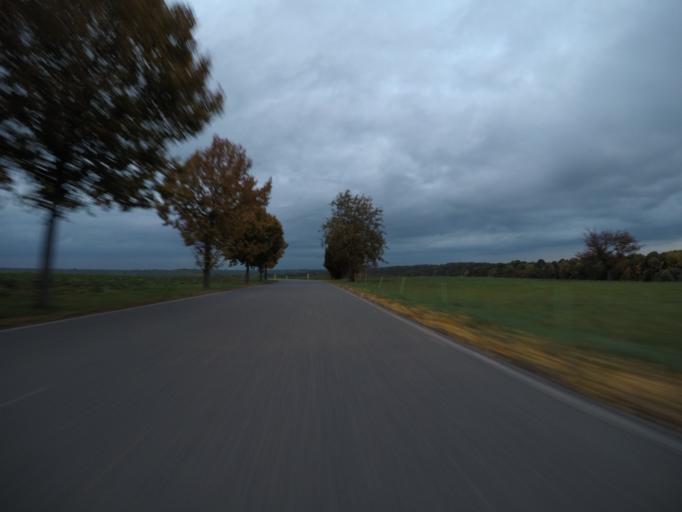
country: DE
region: Thuringia
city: Saara
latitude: 50.9116
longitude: 12.4018
